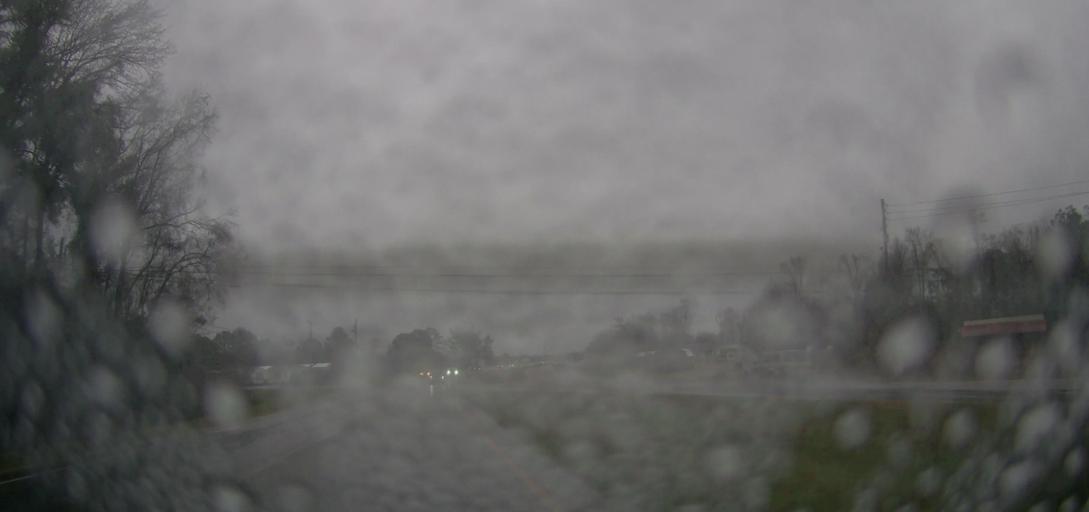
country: US
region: Alabama
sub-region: Autauga County
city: Prattville
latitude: 32.4287
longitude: -86.4139
